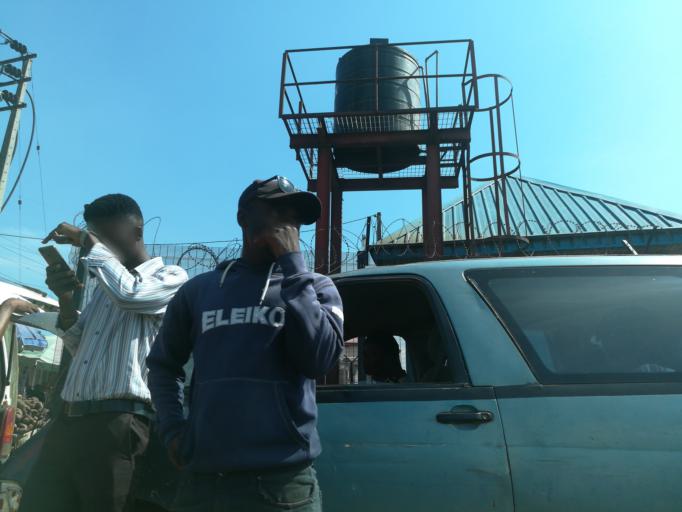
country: NG
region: Lagos
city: Ebute Ikorodu
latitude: 6.6246
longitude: 3.4832
